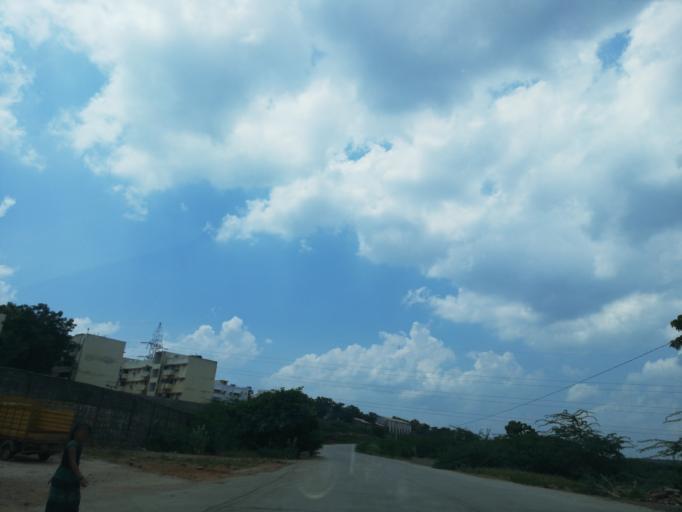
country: IN
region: Andhra Pradesh
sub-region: Guntur
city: Macherla
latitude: 16.5827
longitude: 79.3282
